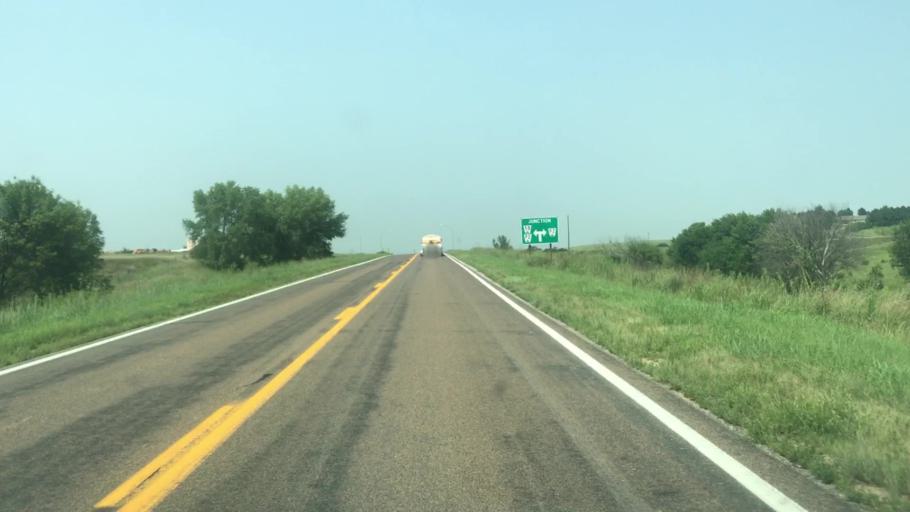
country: US
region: Nebraska
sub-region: Sherman County
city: Loup City
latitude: 41.2595
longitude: -98.9388
